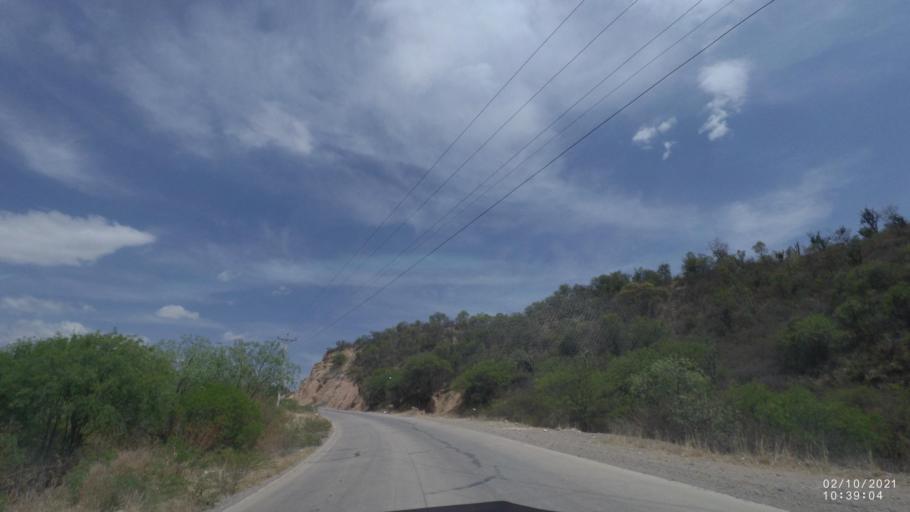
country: BO
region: Cochabamba
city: Capinota
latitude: -17.6298
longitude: -66.2702
